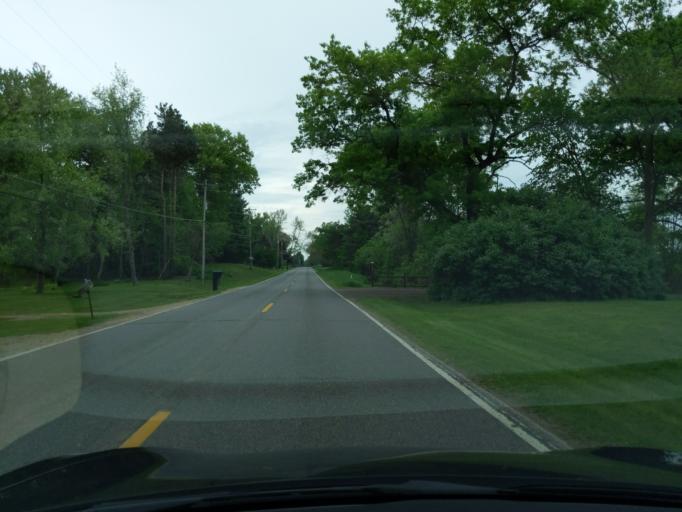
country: US
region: Michigan
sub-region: Ingham County
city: Leslie
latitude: 42.3731
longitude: -84.3491
